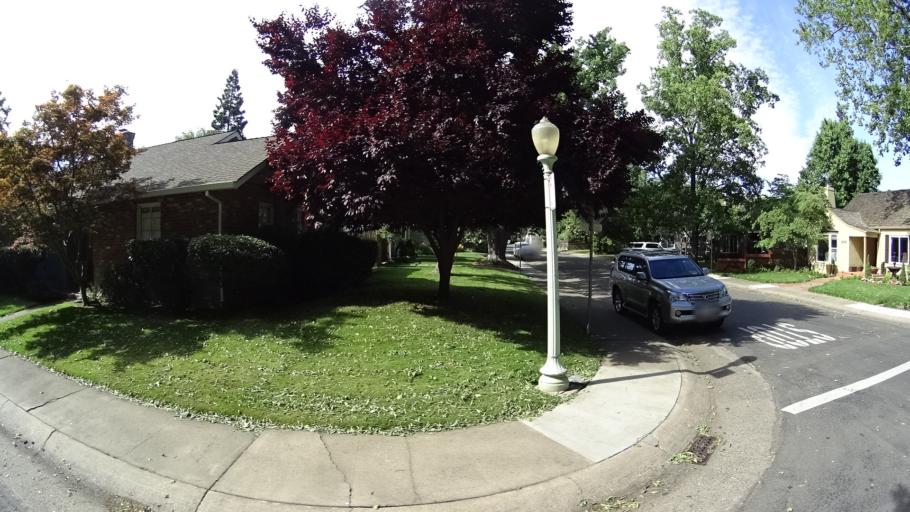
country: US
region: California
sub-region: Sacramento County
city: Sacramento
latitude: 38.5477
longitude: -121.4930
